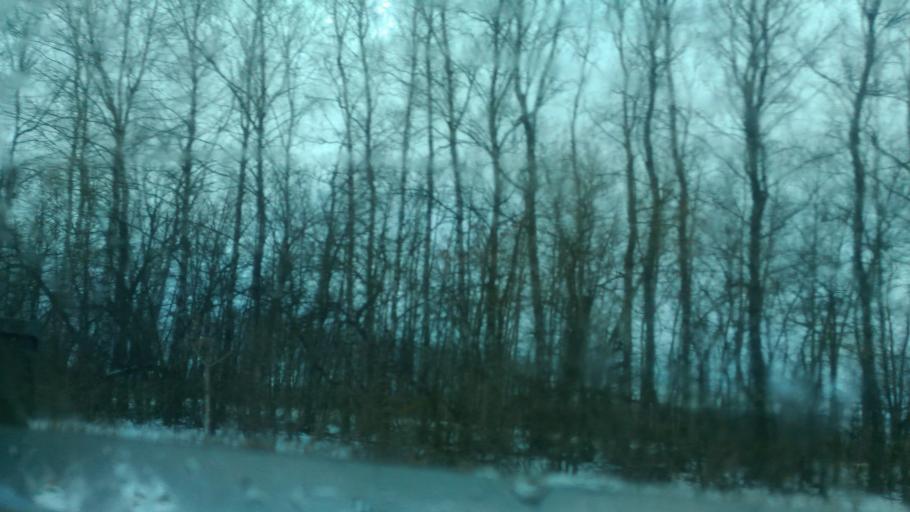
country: RU
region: Tula
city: Bolokhovo
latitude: 54.0915
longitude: 37.7720
